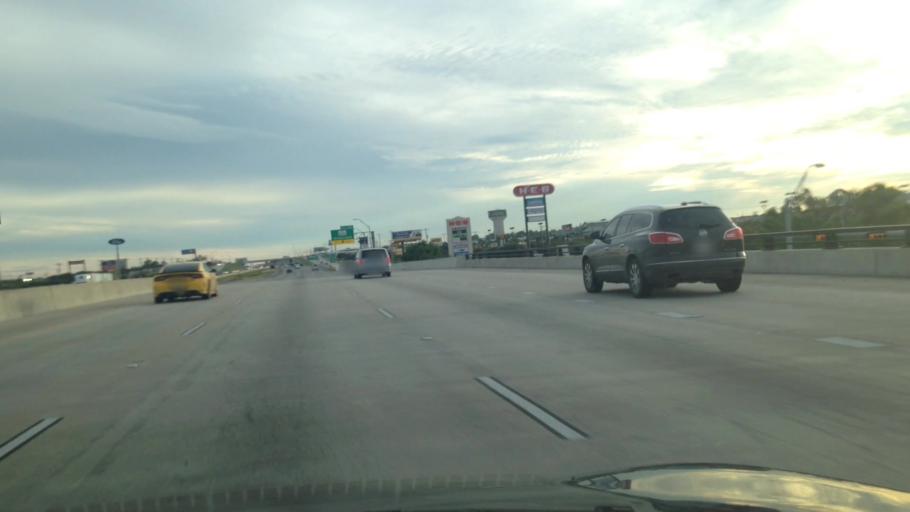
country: US
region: Texas
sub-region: Hays County
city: Buda
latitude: 30.0890
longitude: -97.8188
